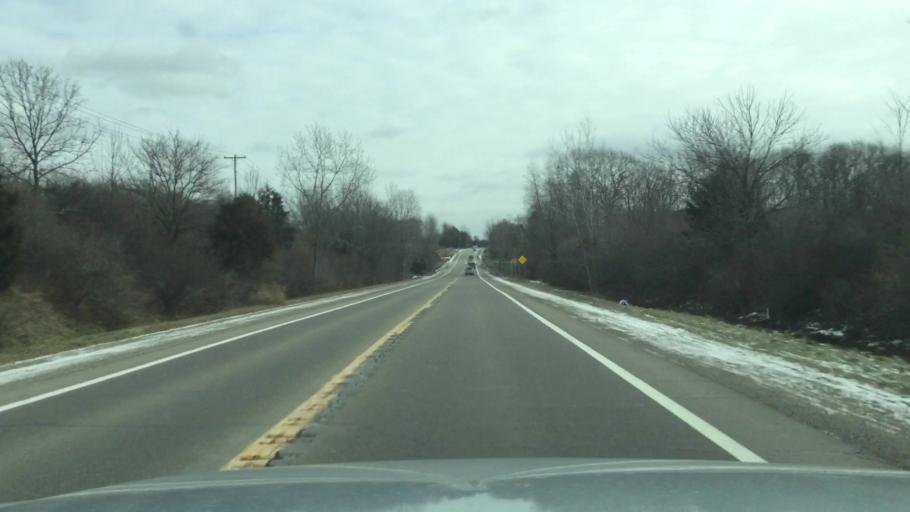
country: US
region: Michigan
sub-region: Genesee County
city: Montrose
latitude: 43.1767
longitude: -83.8599
